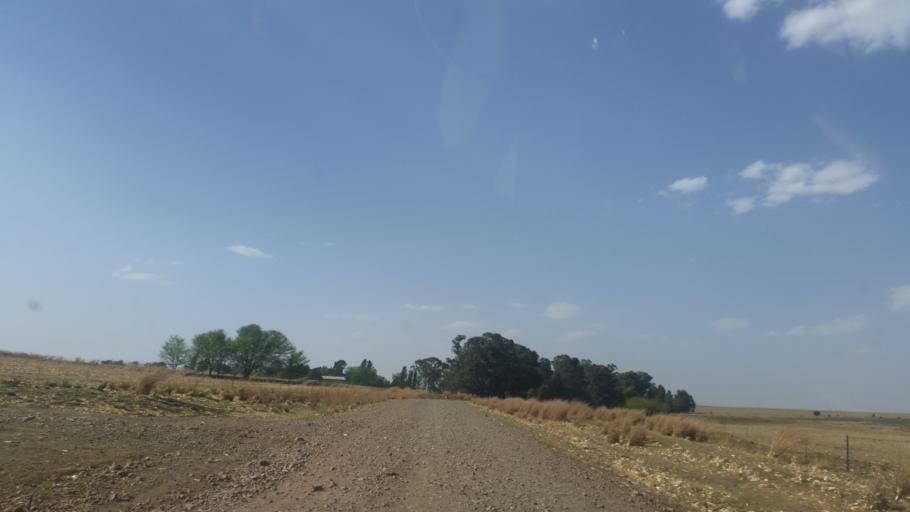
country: ZA
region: Orange Free State
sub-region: Thabo Mofutsanyana District Municipality
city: Phuthaditjhaba
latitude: -28.2408
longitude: 28.6679
